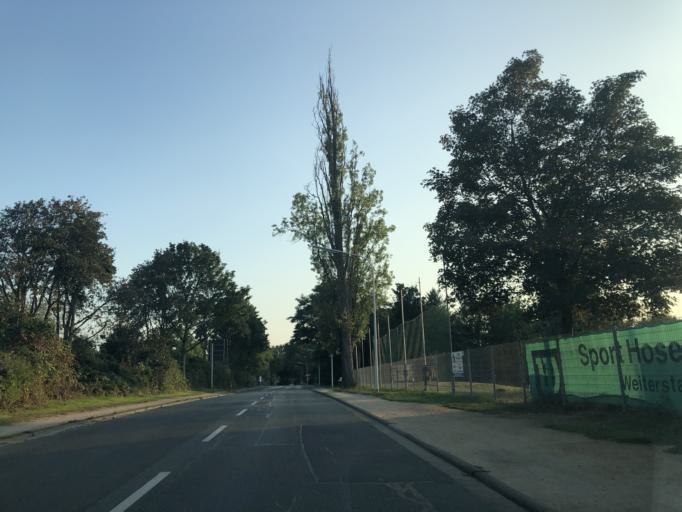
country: DE
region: Hesse
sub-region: Regierungsbezirk Darmstadt
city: Darmstadt
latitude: 49.8916
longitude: 8.6737
